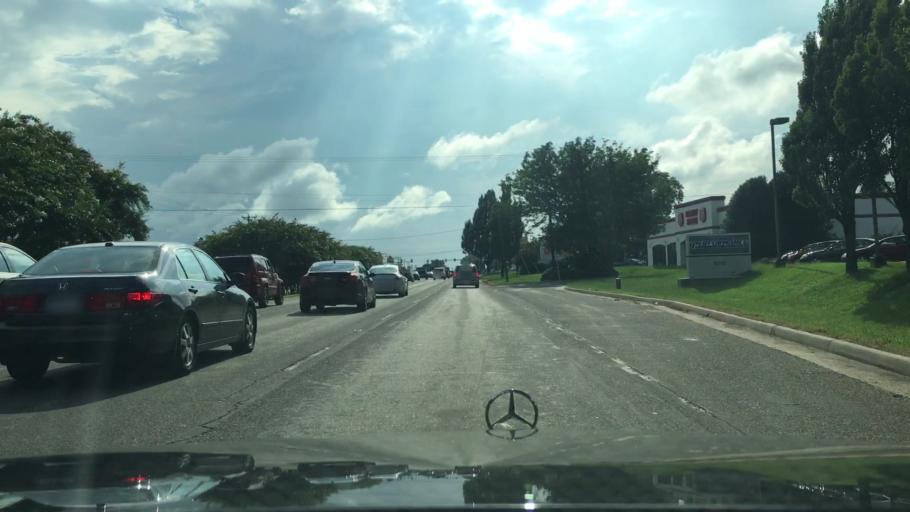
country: US
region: Virginia
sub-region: Chesterfield County
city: Bon Air
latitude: 37.5066
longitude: -77.5989
